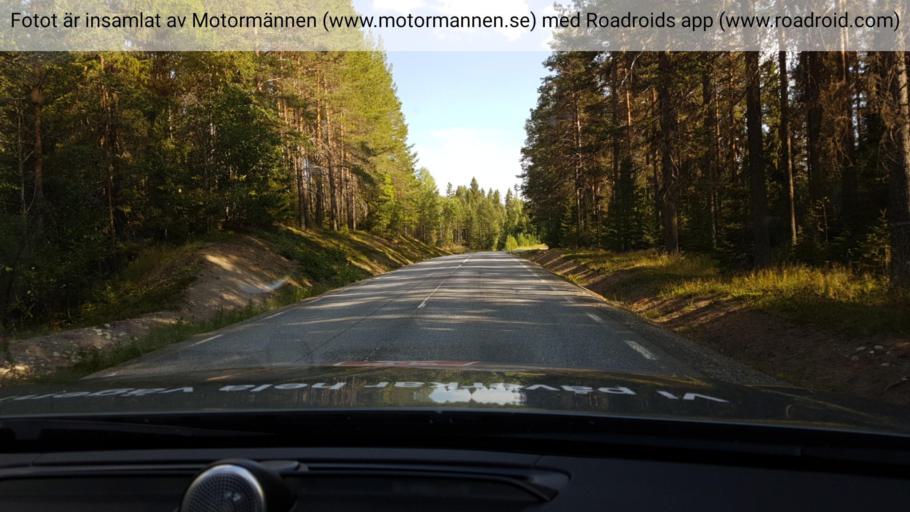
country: SE
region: Vaesterbotten
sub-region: Dorotea Kommun
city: Dorotea
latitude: 63.9016
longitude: 16.3579
